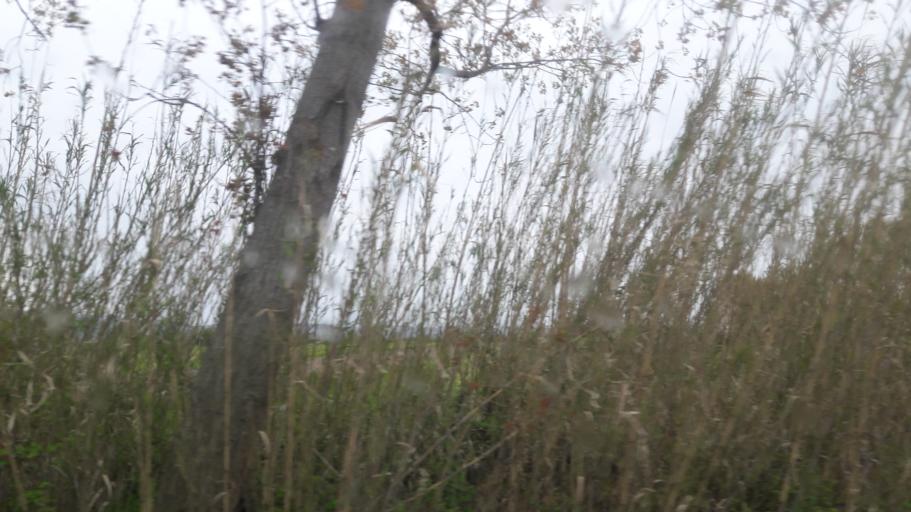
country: AL
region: Shkoder
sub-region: Rrethi i Shkodres
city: Berdica e Madhe
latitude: 41.9662
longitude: 19.4992
